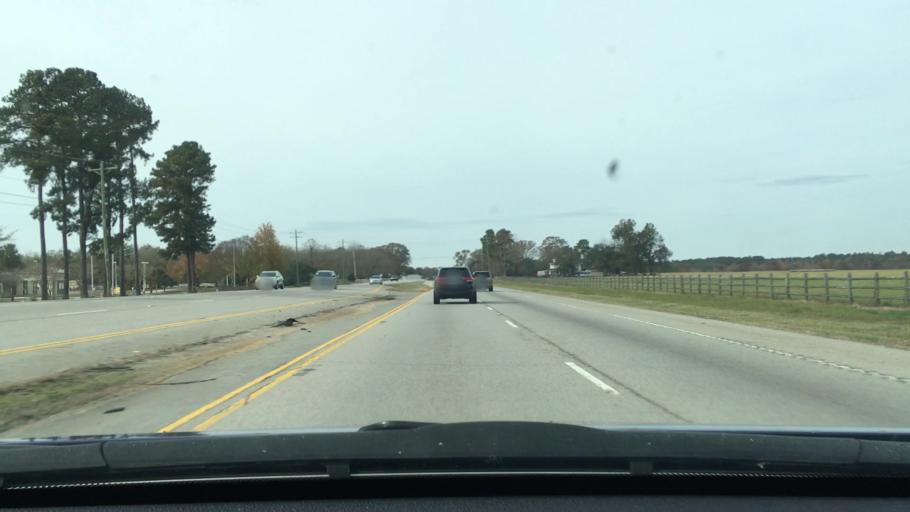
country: US
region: South Carolina
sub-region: Richland County
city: Hopkins
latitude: 33.9422
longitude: -80.8035
